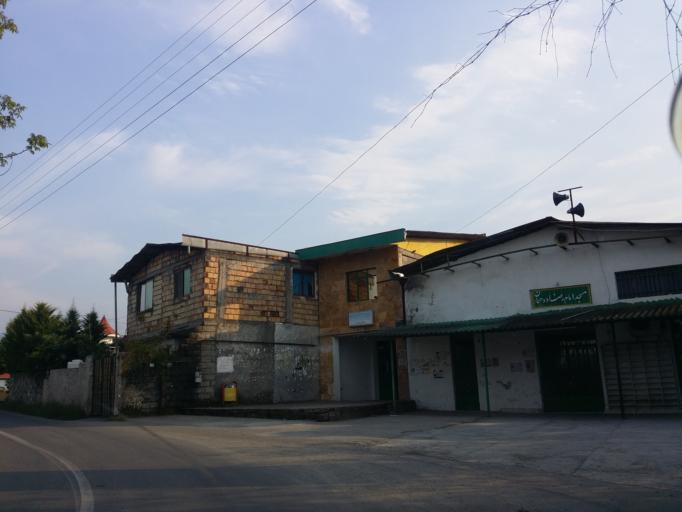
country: IR
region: Mazandaran
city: Chalus
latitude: 36.6875
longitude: 51.3712
